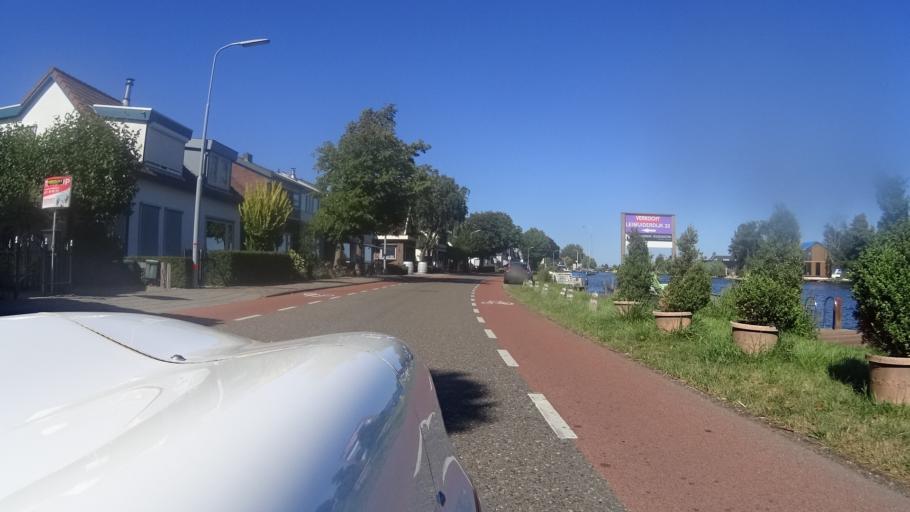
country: NL
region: North Holland
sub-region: Gemeente Aalsmeer
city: Aalsmeer
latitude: 52.2555
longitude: 4.7125
